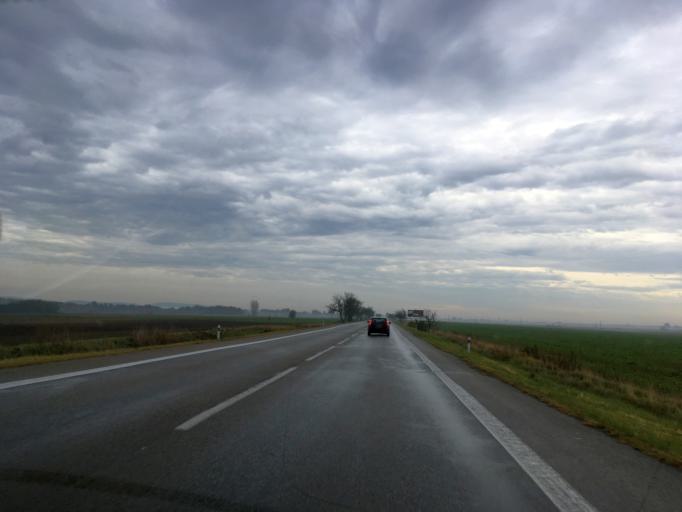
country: SK
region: Nitriansky
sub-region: Okres Komarno
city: Hurbanovo
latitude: 47.8269
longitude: 18.1750
